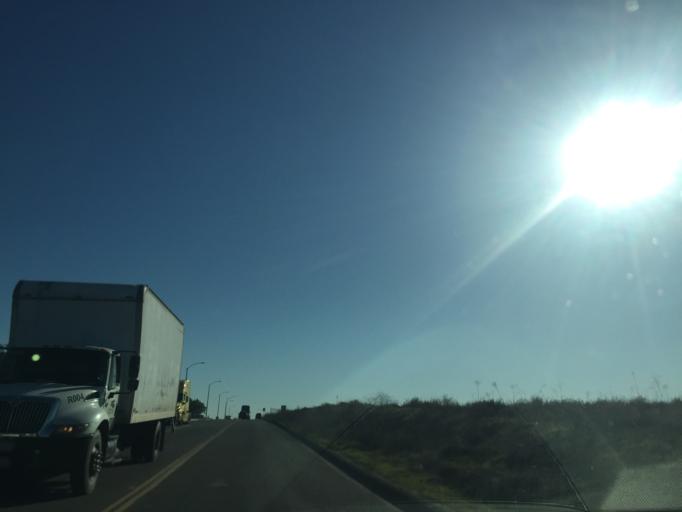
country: MX
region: Baja California
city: Tijuana
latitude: 32.5672
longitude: -116.9278
